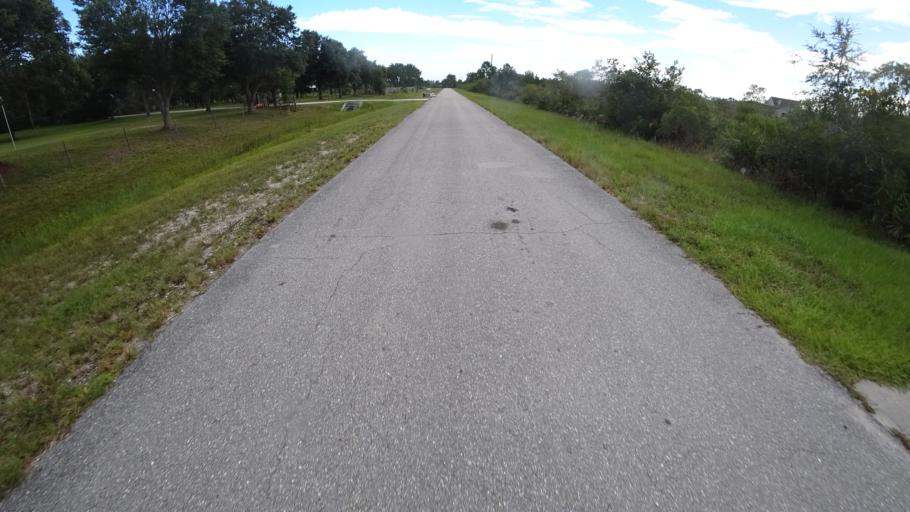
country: US
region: Florida
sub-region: Sarasota County
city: The Meadows
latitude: 27.4133
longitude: -82.2751
